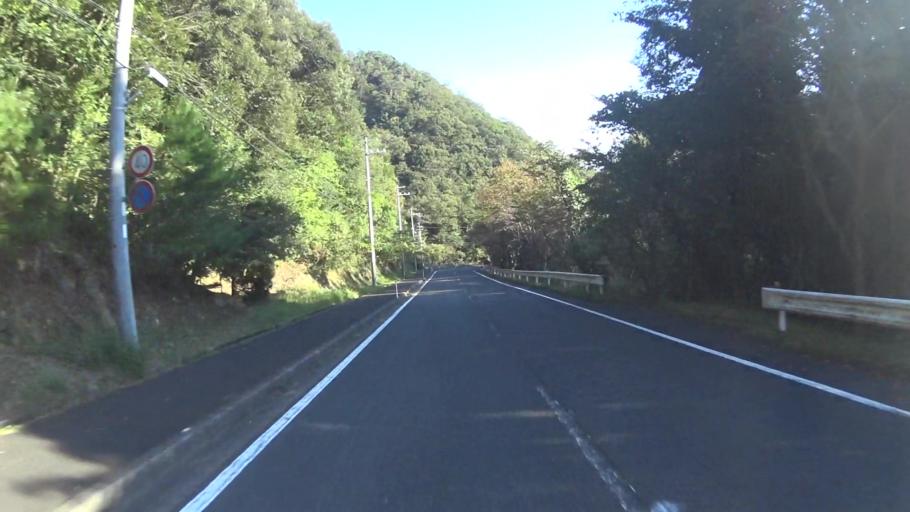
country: JP
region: Hyogo
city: Toyooka
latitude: 35.6158
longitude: 134.8842
